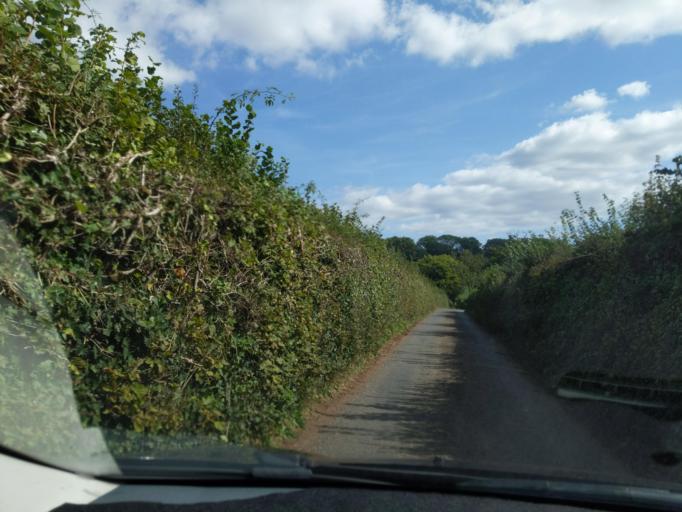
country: GB
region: England
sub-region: Devon
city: Marldon
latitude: 50.4605
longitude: -3.6164
